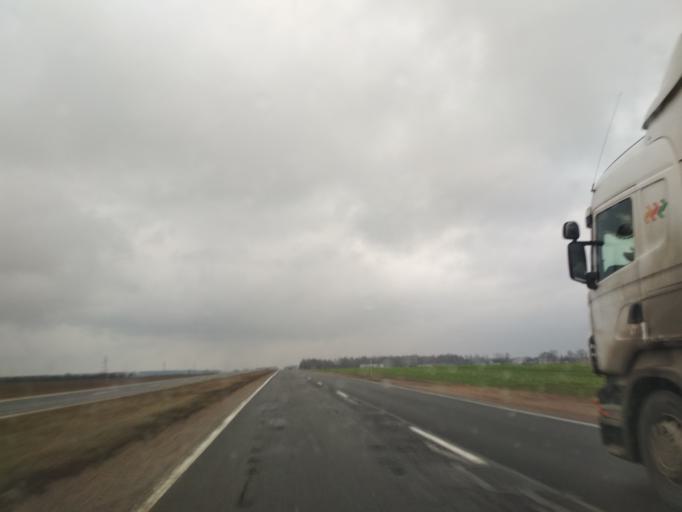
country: BY
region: Minsk
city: Dukora
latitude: 53.6406
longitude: 27.9977
